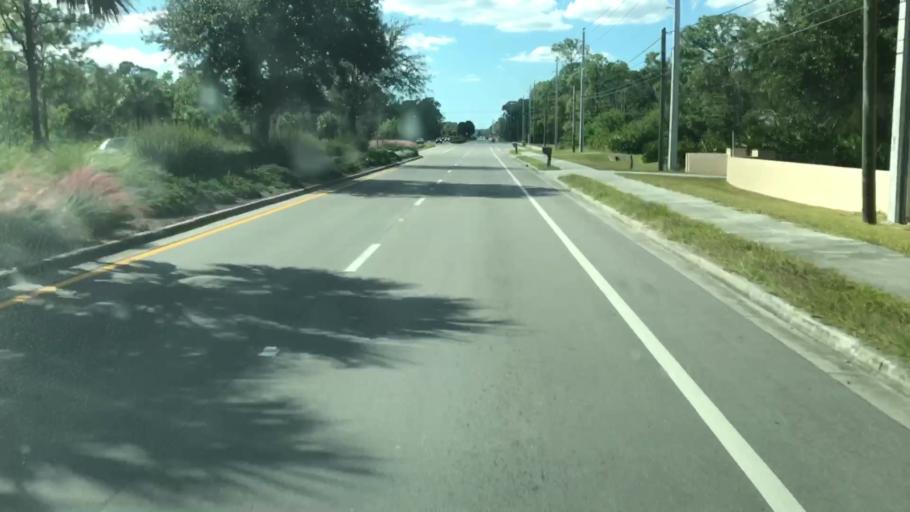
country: US
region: Florida
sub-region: Collier County
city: Vineyards
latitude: 26.2292
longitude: -81.6634
